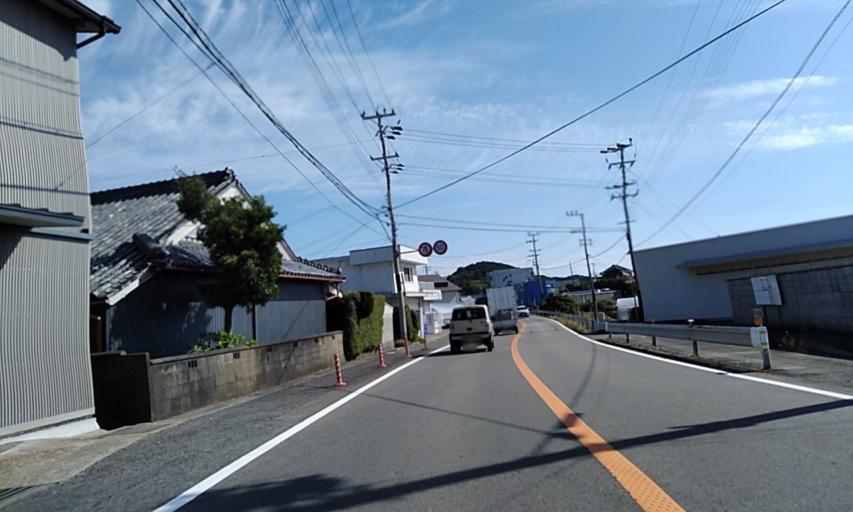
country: JP
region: Wakayama
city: Gobo
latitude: 33.8564
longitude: 135.1633
